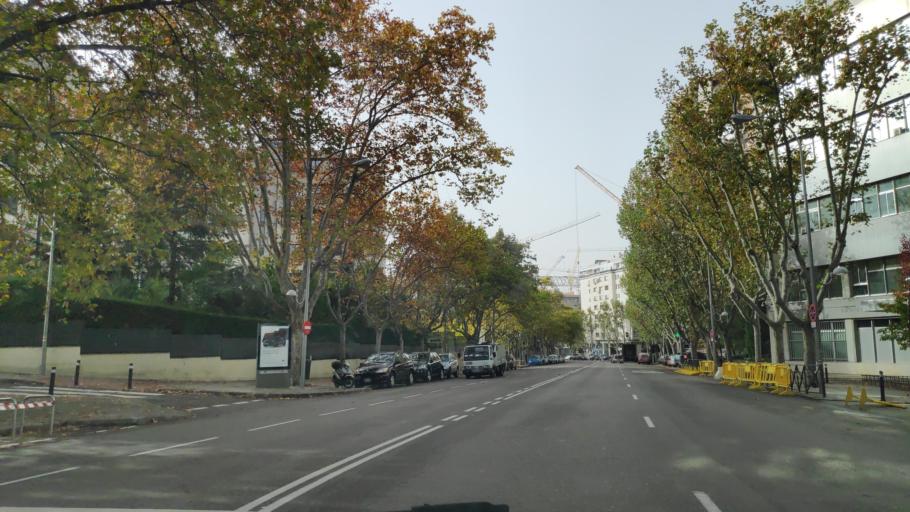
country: ES
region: Madrid
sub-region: Provincia de Madrid
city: Chamartin
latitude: 40.4574
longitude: -3.6857
